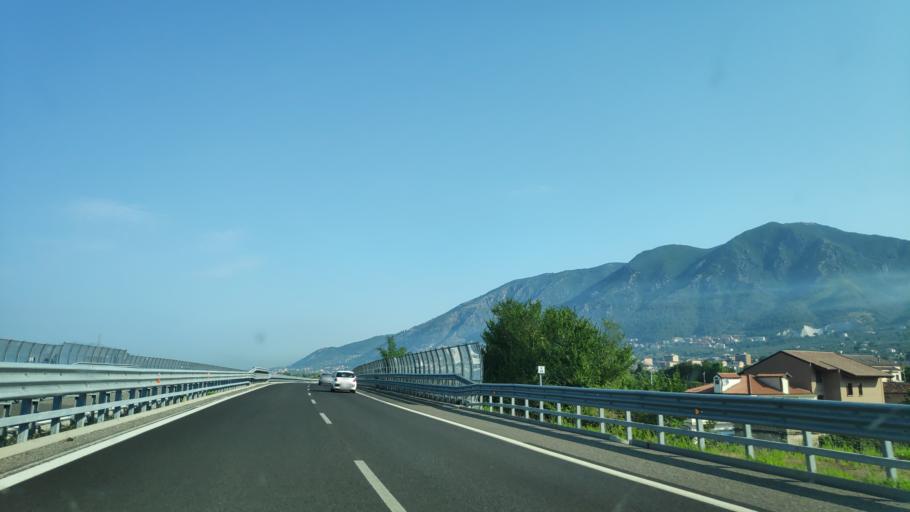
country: IT
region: Campania
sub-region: Provincia di Salerno
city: Sala Consilina
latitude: 40.3687
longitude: 15.6020
